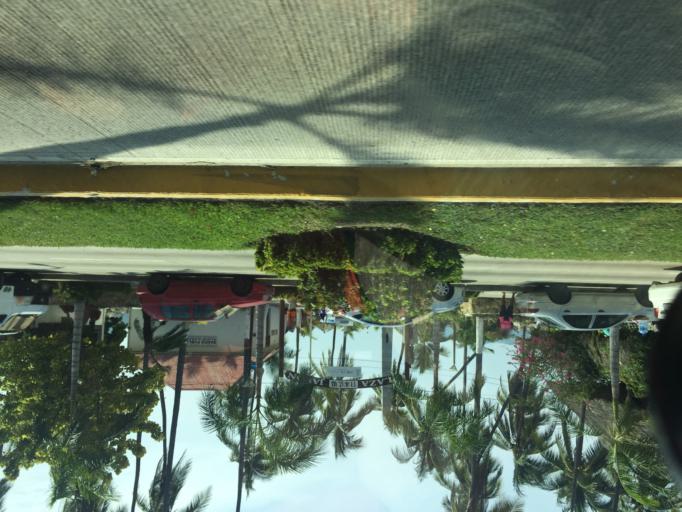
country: MX
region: Guerrero
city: Acapulco de Juarez
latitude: 16.8576
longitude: -99.8916
